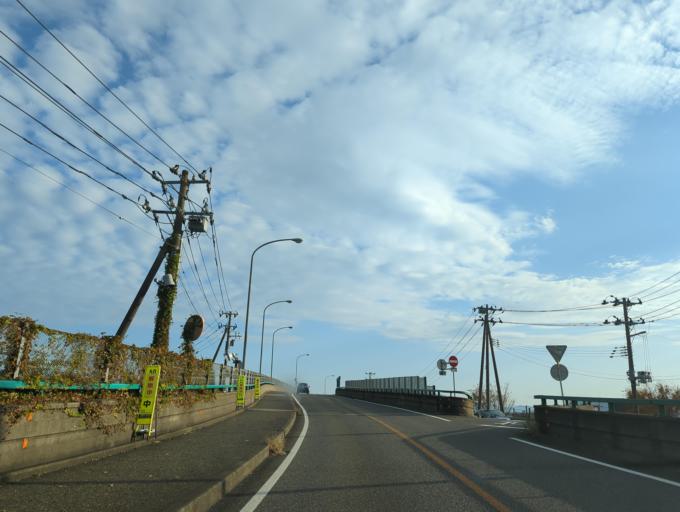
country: JP
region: Niigata
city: Kashiwazaki
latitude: 37.3663
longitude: 138.5628
